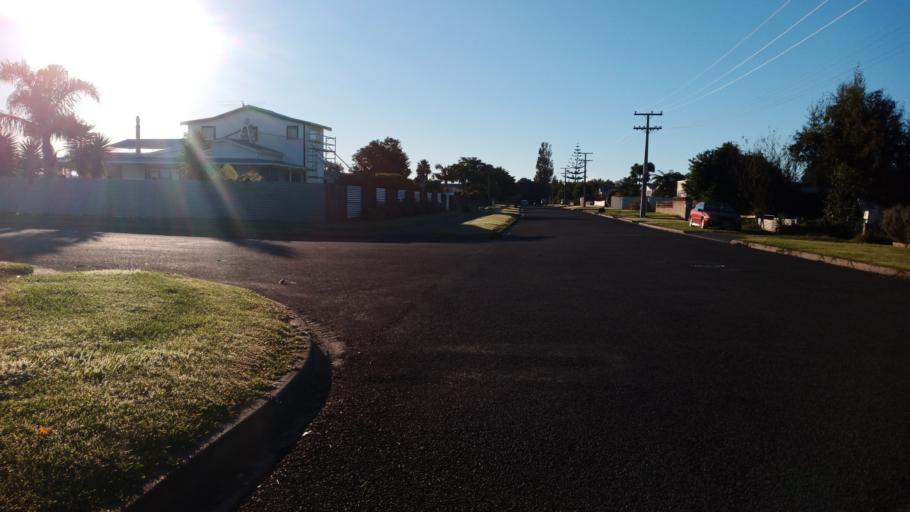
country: NZ
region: Gisborne
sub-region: Gisborne District
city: Gisborne
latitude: -38.6619
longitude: 177.9886
